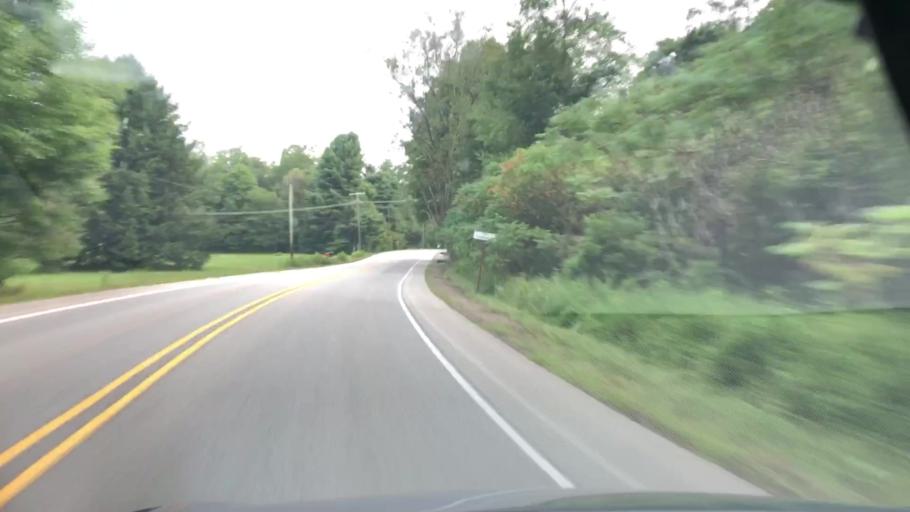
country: US
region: Pennsylvania
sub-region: Venango County
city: Hasson Heights
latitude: 41.5121
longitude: -79.7030
